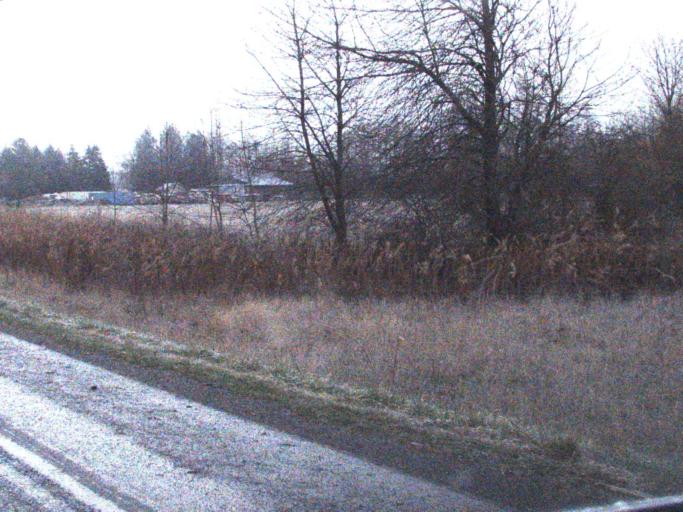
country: US
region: Washington
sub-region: Skagit County
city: Sedro-Woolley
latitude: 48.5271
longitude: -121.9714
